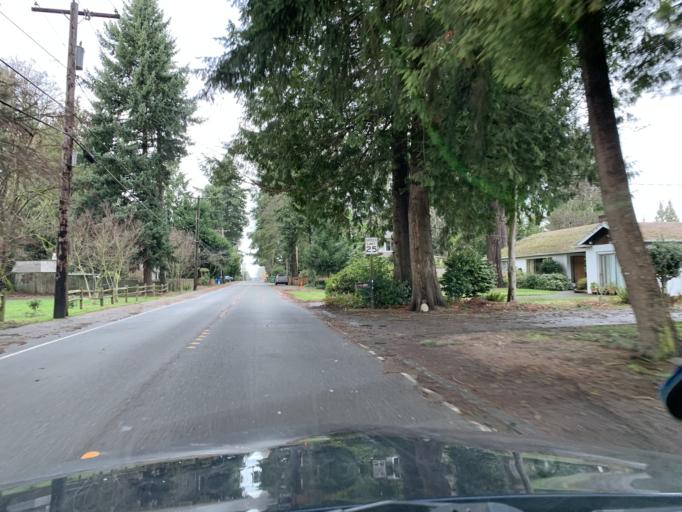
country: US
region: Washington
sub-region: King County
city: Mercer Island
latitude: 47.5822
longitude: -122.2431
